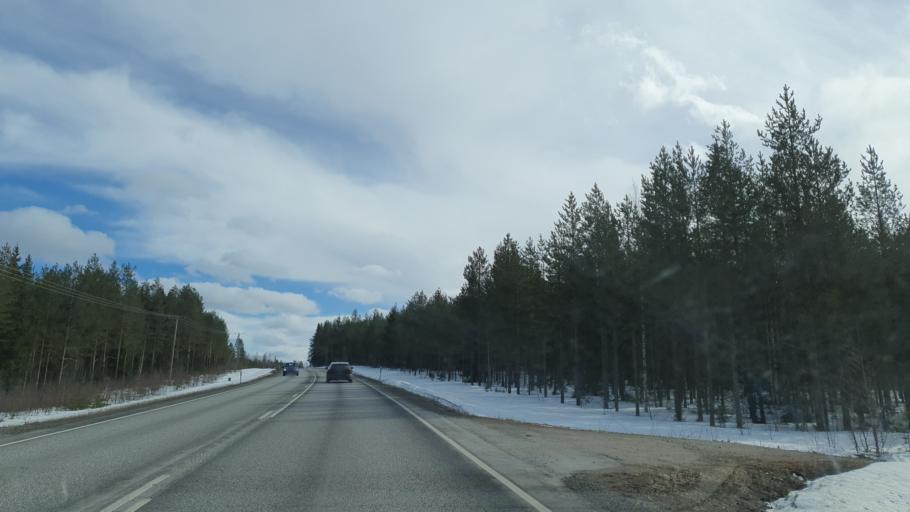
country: FI
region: Kainuu
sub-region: Kajaani
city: Paltamo
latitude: 64.3716
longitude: 28.0333
